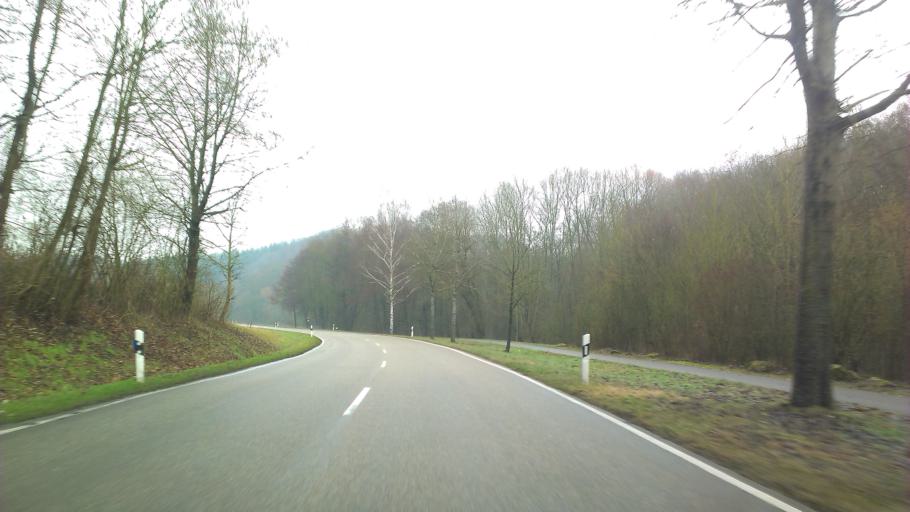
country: DE
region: Baden-Wuerttemberg
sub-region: Karlsruhe Region
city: Muhlhausen
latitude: 49.2502
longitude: 8.7460
